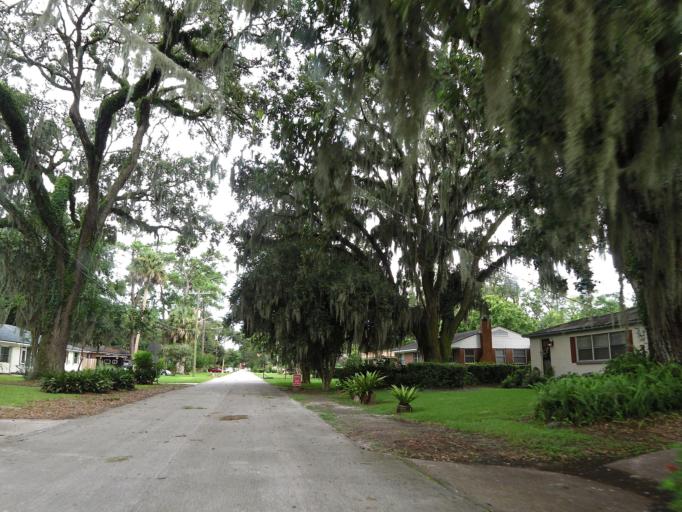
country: US
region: Florida
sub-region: Duval County
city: Jacksonville
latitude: 30.3116
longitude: -81.6194
